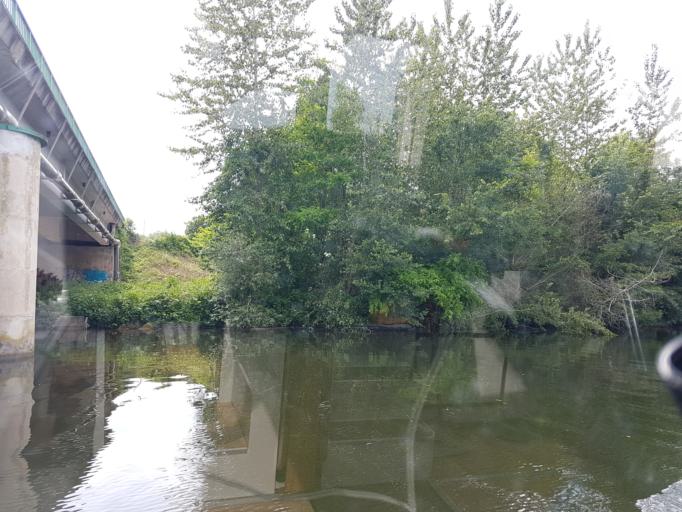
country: FR
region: Bourgogne
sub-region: Departement de l'Yonne
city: Gurgy
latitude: 47.8567
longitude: 3.5569
